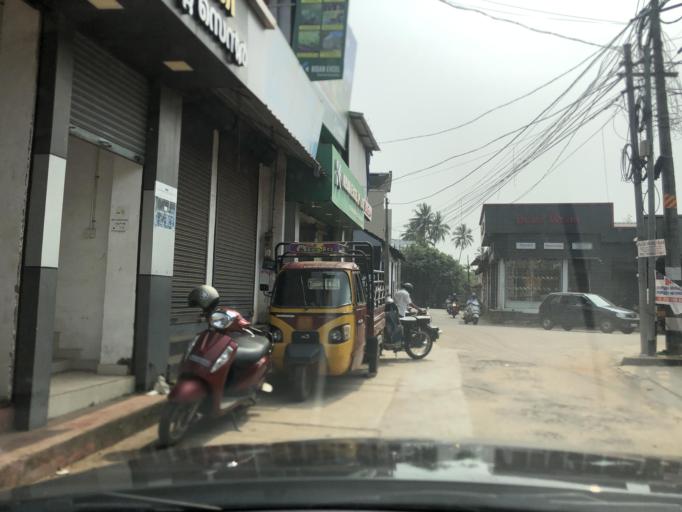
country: IN
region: Kerala
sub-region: Kozhikode
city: Kozhikode
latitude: 11.2518
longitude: 75.7746
